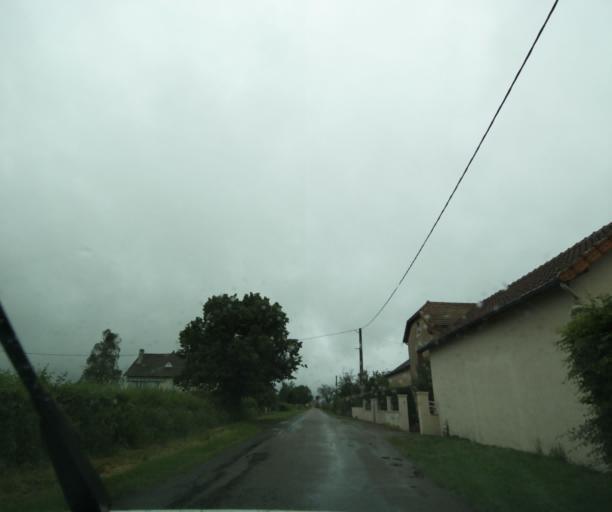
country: FR
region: Bourgogne
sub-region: Departement de Saone-et-Loire
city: Charolles
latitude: 46.4250
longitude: 4.2981
